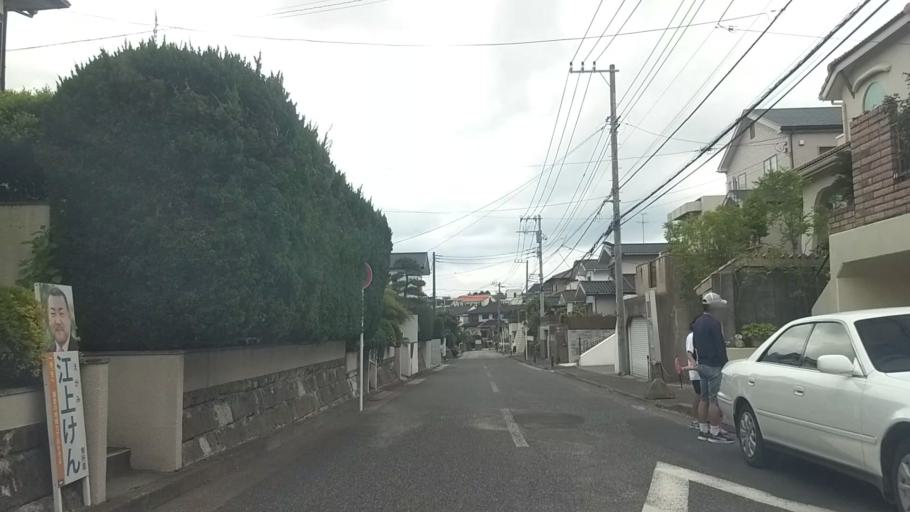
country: JP
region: Kanagawa
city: Fujisawa
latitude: 35.3556
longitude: 139.5068
